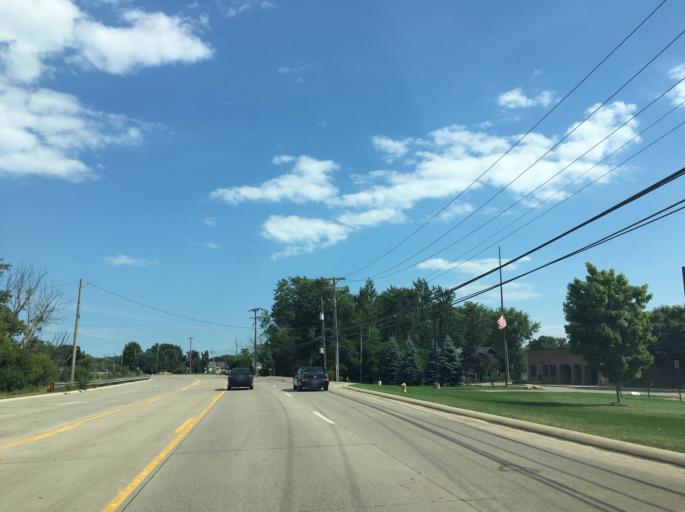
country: US
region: Michigan
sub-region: Macomb County
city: Clinton
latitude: 42.6078
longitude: -82.9223
